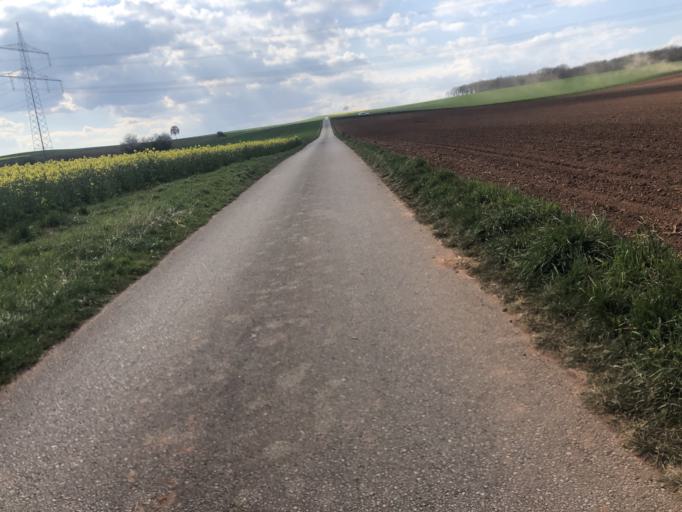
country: DE
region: North Rhine-Westphalia
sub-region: Regierungsbezirk Koln
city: Mechernich
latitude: 50.6092
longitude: 6.5869
